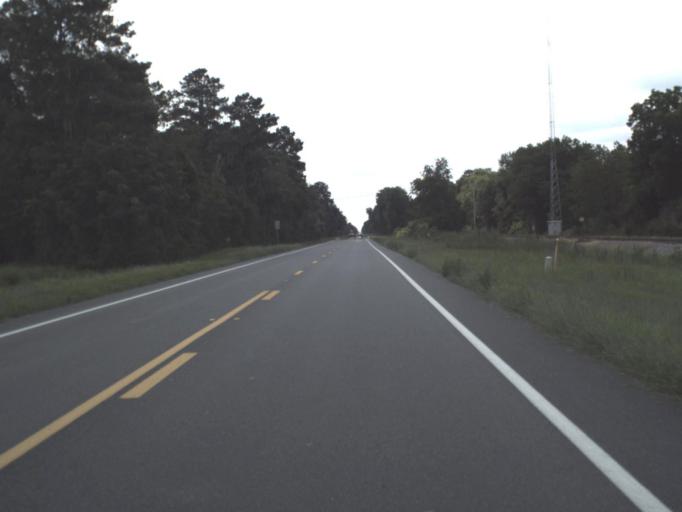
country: US
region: Florida
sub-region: Hamilton County
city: Jasper
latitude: 30.4019
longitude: -82.8369
